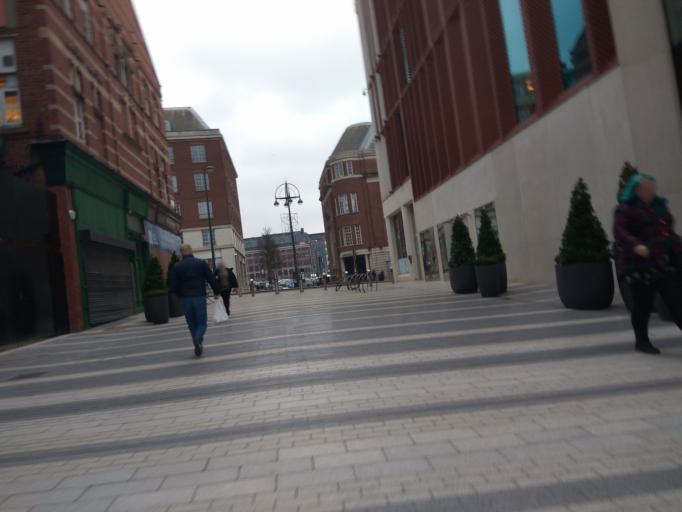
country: GB
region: England
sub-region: City and Borough of Leeds
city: Leeds
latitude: 53.7984
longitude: -1.5391
